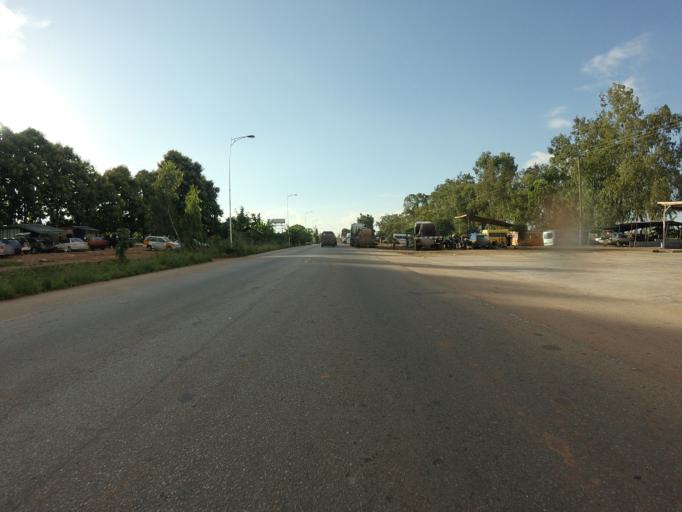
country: GH
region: Ashanti
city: Tafo
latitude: 6.9221
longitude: -1.6614
